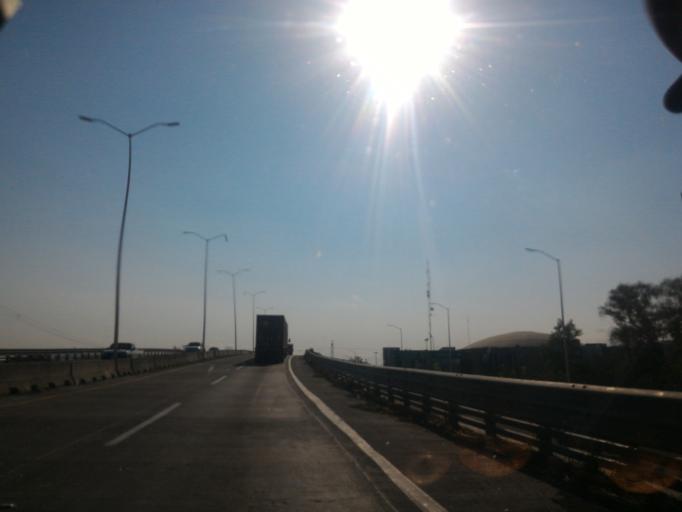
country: MX
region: Colima
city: Colima
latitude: 19.2562
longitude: -103.6858
